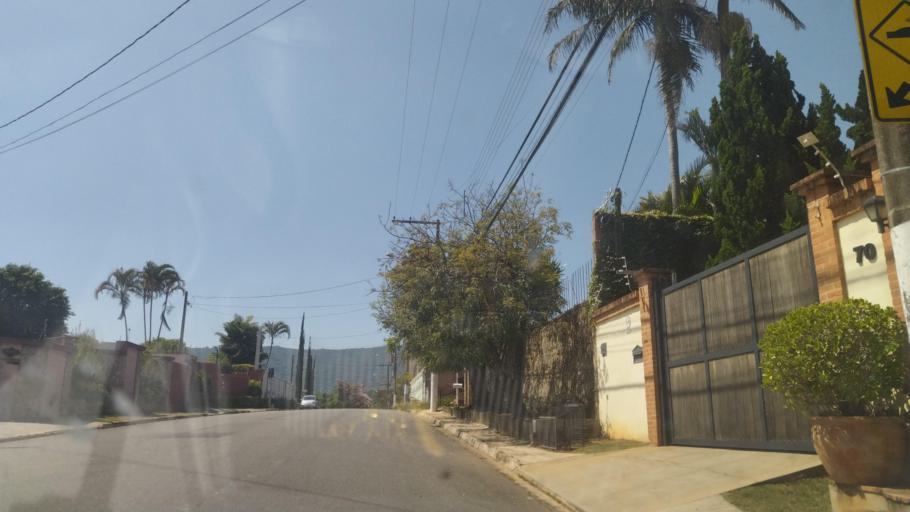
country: BR
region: Sao Paulo
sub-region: Atibaia
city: Atibaia
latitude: -23.1246
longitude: -46.5470
